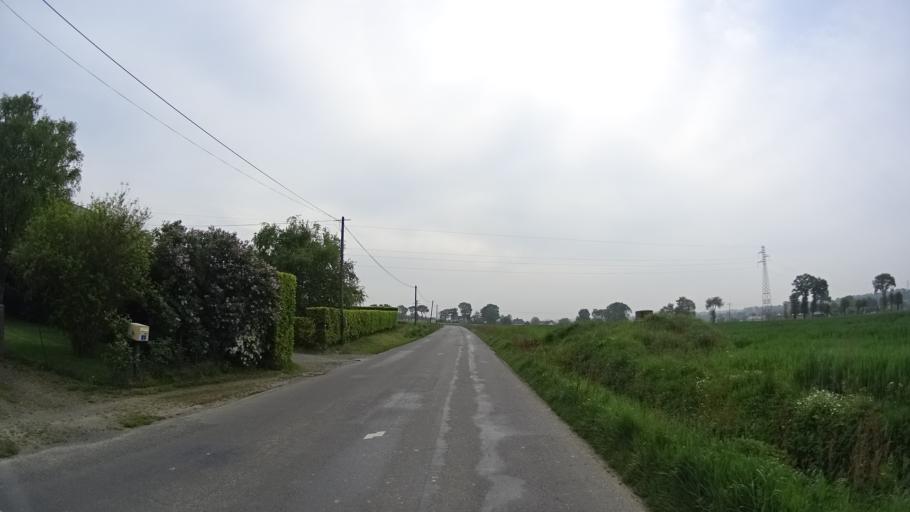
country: FR
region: Brittany
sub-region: Departement d'Ille-et-Vilaine
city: Montreuil-le-Gast
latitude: 48.2478
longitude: -1.7387
